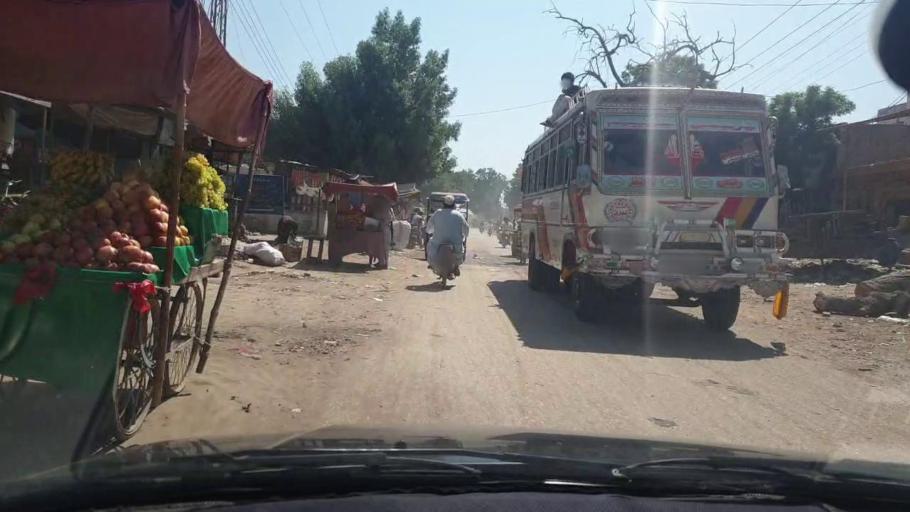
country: PK
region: Sindh
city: Tando Allahyar
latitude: 25.4540
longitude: 68.7226
